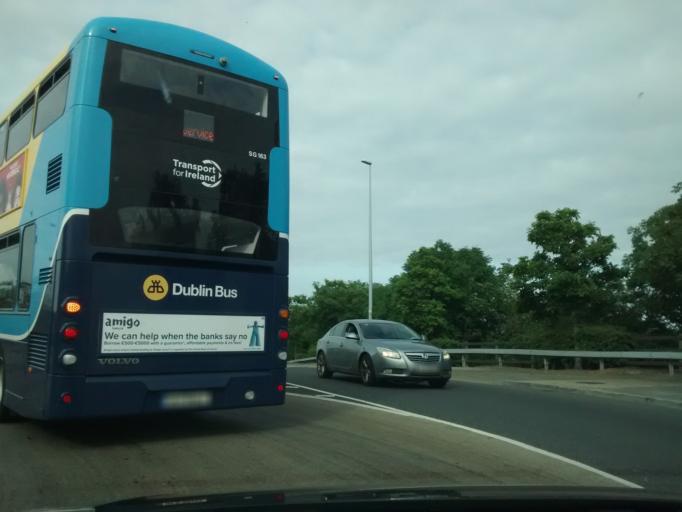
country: IE
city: Cherry Orchard
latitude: 53.3160
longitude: -6.3728
